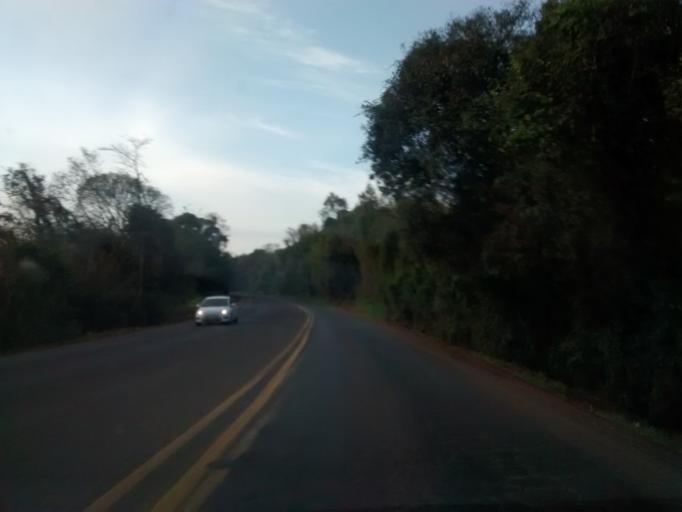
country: BR
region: Parana
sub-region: Francisco Beltrao
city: Francisco Beltrao
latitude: -26.1302
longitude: -53.0400
